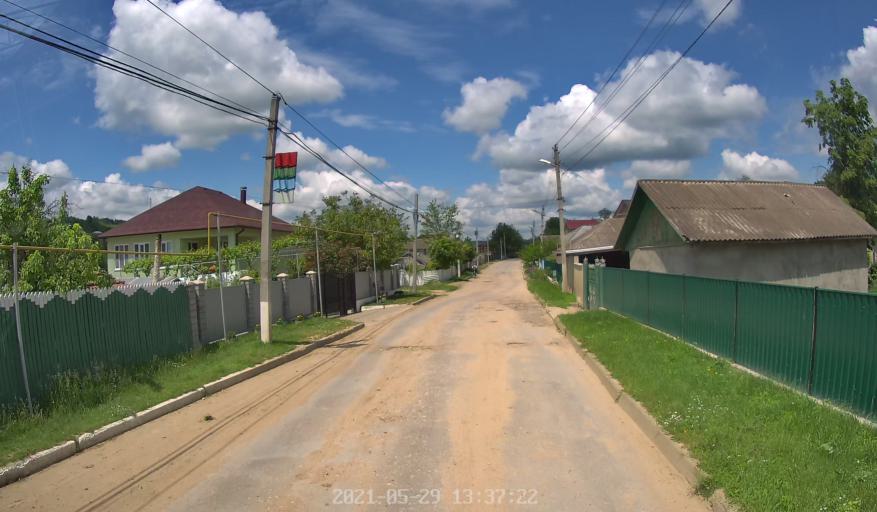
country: MD
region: Hincesti
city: Hincesti
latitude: 46.8279
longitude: 28.6767
